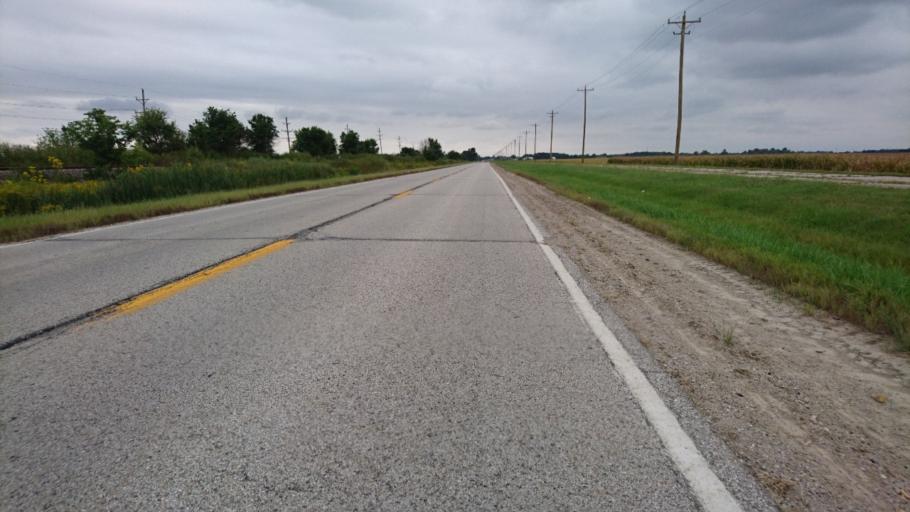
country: US
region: Illinois
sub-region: Livingston County
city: Pontiac
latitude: 40.9144
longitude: -88.6083
